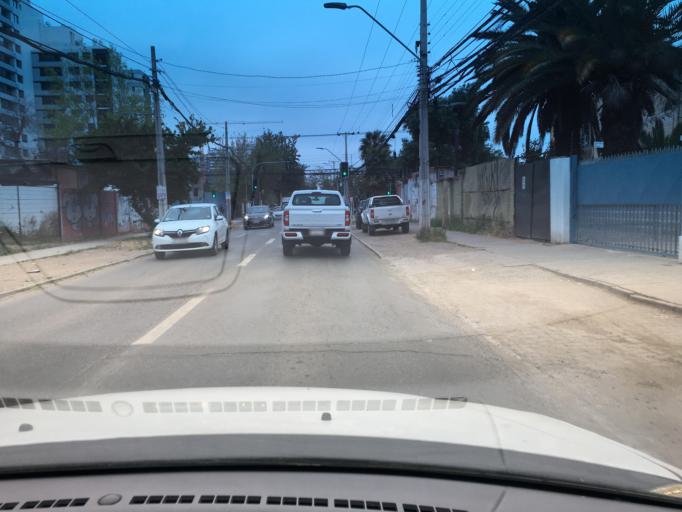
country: CL
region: Santiago Metropolitan
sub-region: Provincia de Santiago
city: Villa Presidente Frei, Nunoa, Santiago, Chile
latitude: -33.4789
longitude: -70.6015
